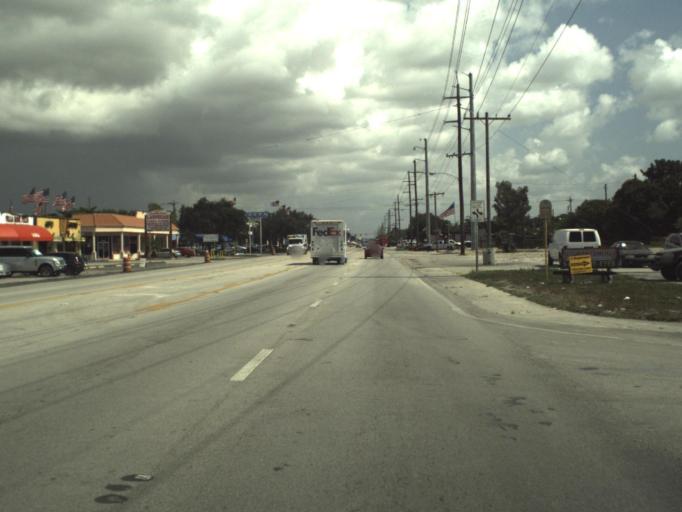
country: US
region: Florida
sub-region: Broward County
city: Pembroke Pines
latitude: 26.0194
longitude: -80.2079
